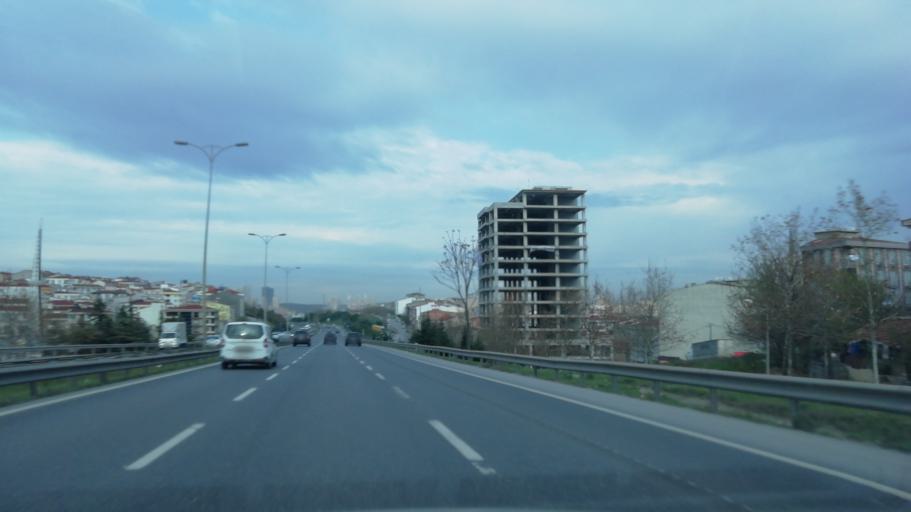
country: TR
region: Istanbul
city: Esenyurt
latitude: 41.0386
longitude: 28.6889
